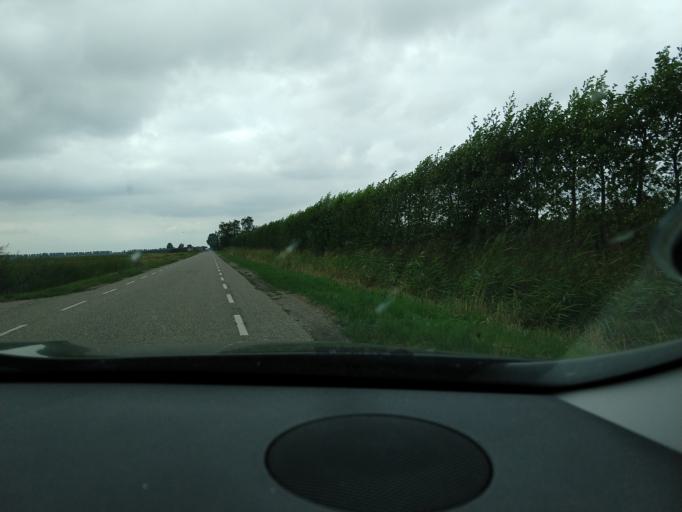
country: NL
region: Zeeland
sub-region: Gemeente Hulst
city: Hulst
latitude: 51.3566
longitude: 4.0720
